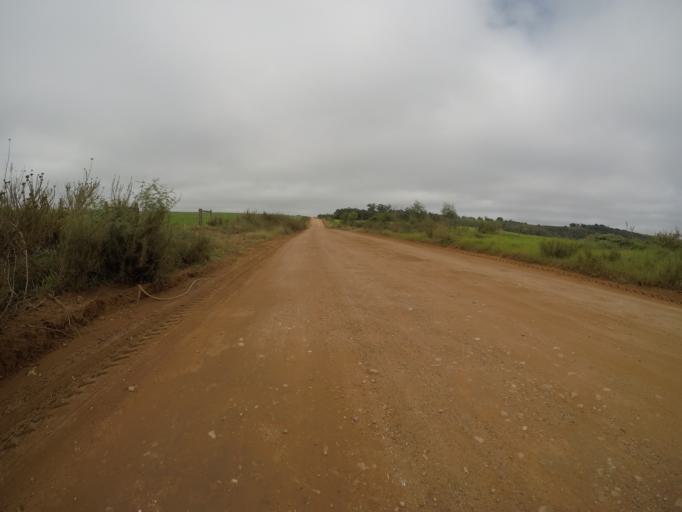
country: ZA
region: Eastern Cape
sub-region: Cacadu District Municipality
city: Kareedouw
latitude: -34.0118
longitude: 24.2371
